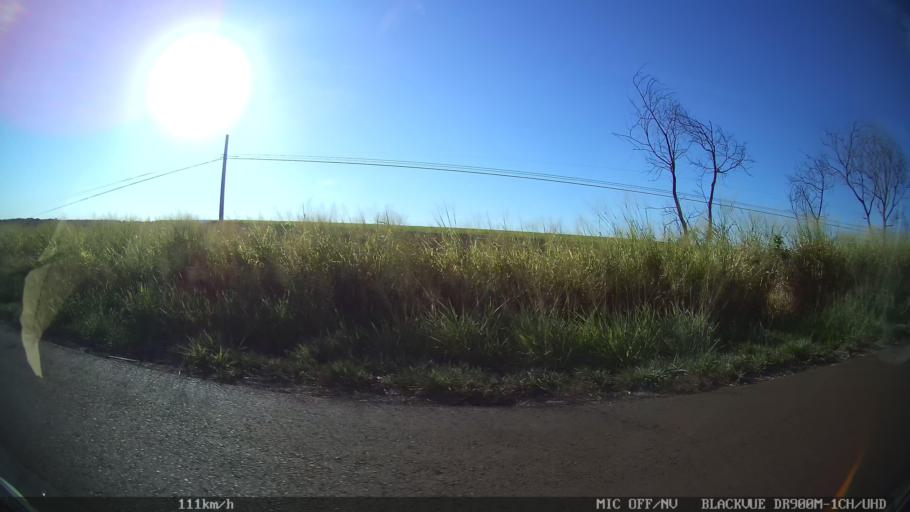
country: BR
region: Sao Paulo
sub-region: Guapiacu
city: Guapiacu
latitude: -20.7392
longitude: -49.0898
